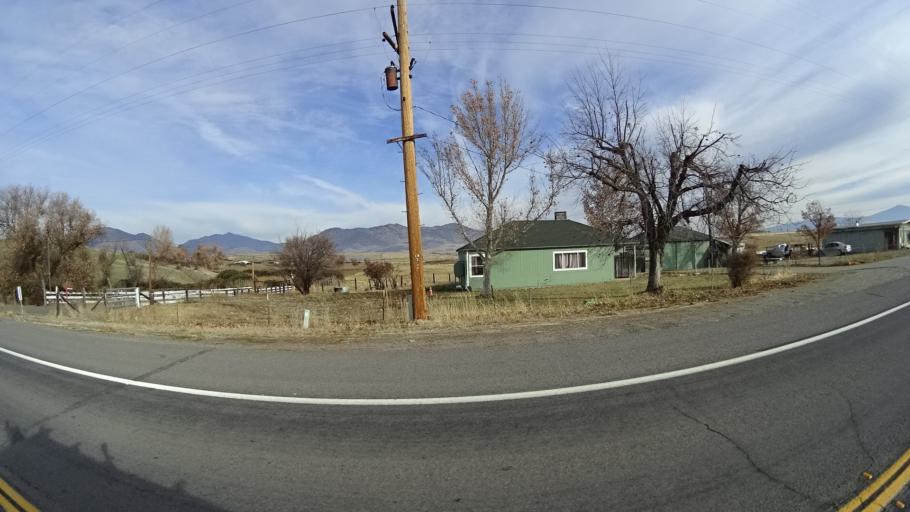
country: US
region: California
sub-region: Siskiyou County
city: Montague
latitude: 41.7289
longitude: -122.5640
